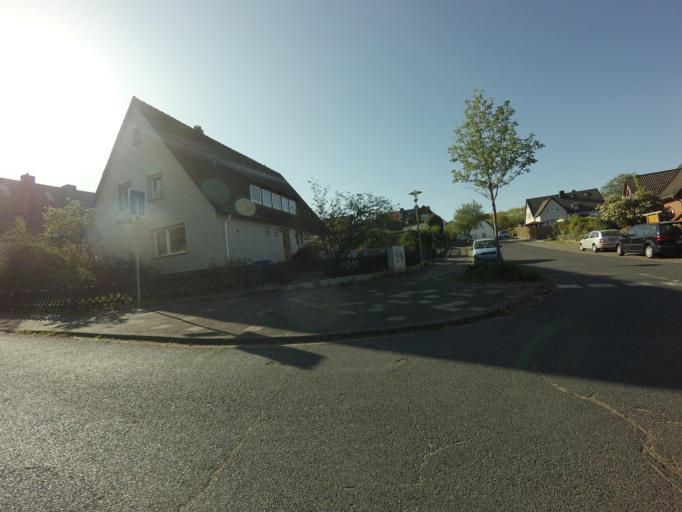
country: DE
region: Lower Saxony
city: Hildesheim
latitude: 52.1396
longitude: 9.9219
